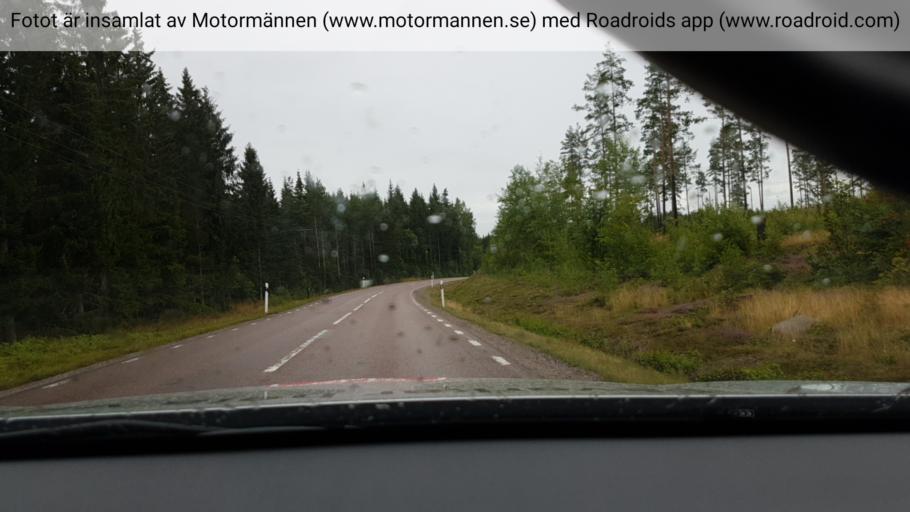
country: SE
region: Gaevleborg
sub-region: Gavle Kommun
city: Hedesunda
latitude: 60.4910
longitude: 16.9359
